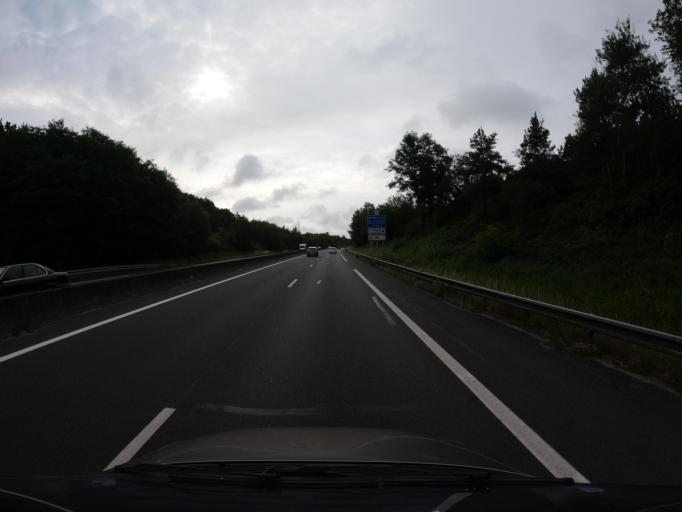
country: FR
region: Centre
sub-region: Departement d'Indre-et-Loire
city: Villandry
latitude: 47.3210
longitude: 0.4947
